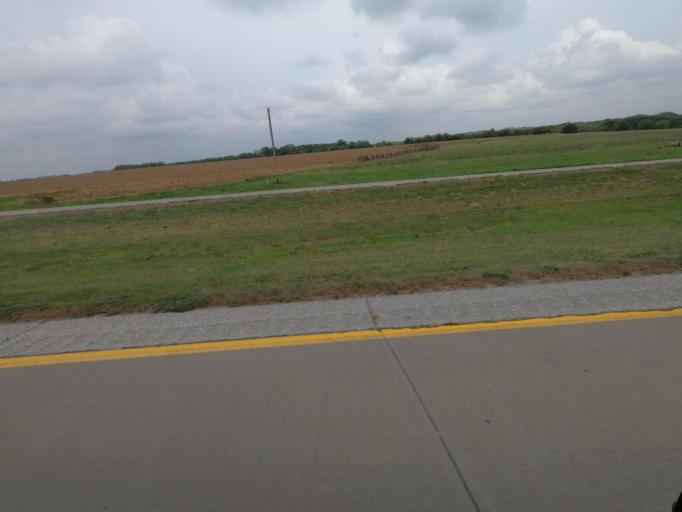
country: US
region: Iowa
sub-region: Wapello County
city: Eddyville
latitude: 41.1225
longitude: -92.5601
